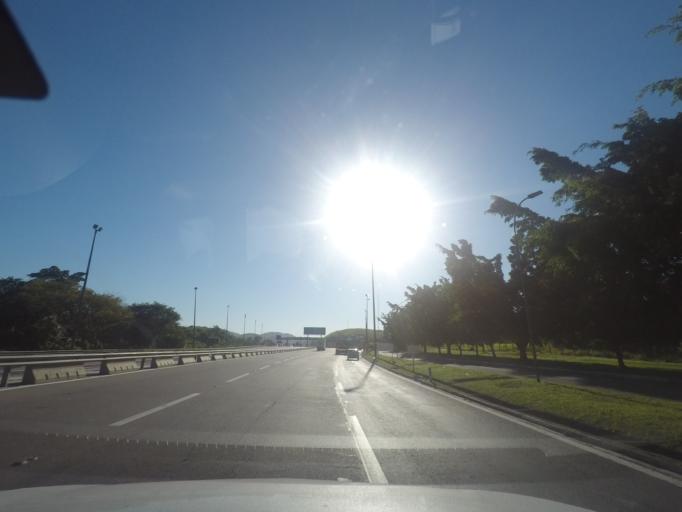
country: BR
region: Rio de Janeiro
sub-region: Petropolis
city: Petropolis
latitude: -22.6470
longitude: -43.1909
